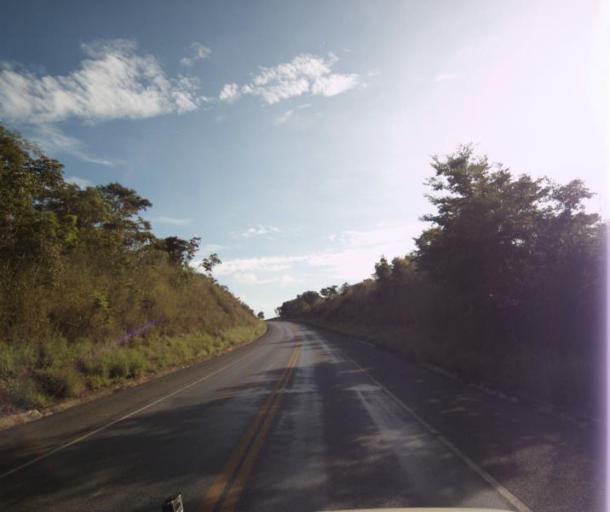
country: BR
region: Goias
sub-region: Pirenopolis
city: Pirenopolis
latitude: -15.5710
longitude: -48.6224
